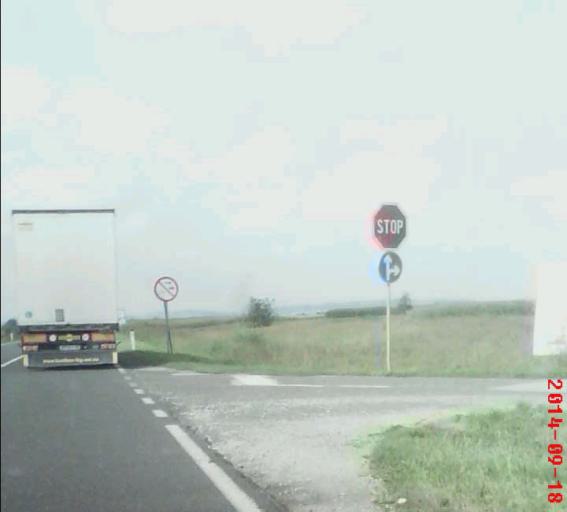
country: SI
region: Podlehnik
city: Podlehnik
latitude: 46.3651
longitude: 15.8671
